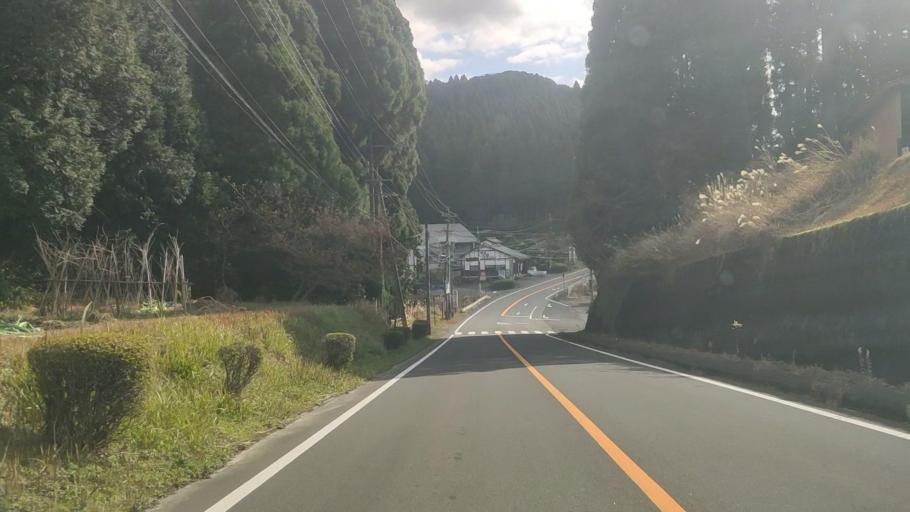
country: JP
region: Kagoshima
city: Kajiki
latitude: 31.8315
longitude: 130.6884
